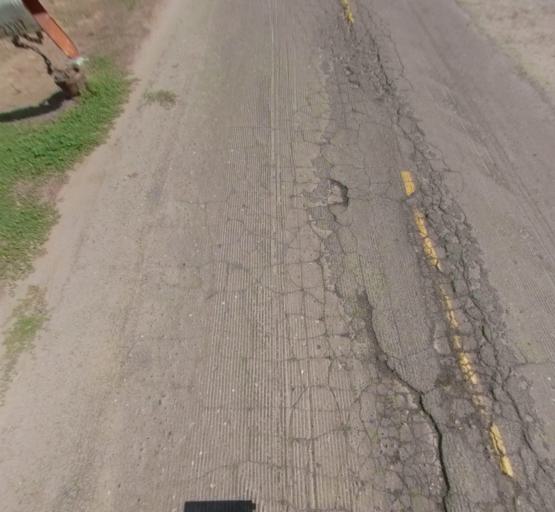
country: US
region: California
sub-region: Madera County
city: Chowchilla
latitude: 37.0876
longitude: -120.2613
